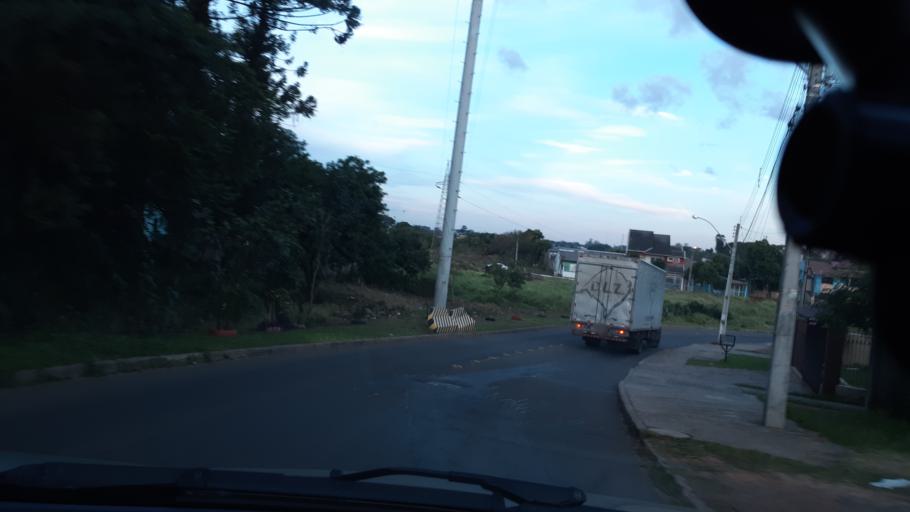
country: BR
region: Rio Grande do Sul
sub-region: Sapucaia Do Sul
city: Sapucaia
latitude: -29.8460
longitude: -51.1468
